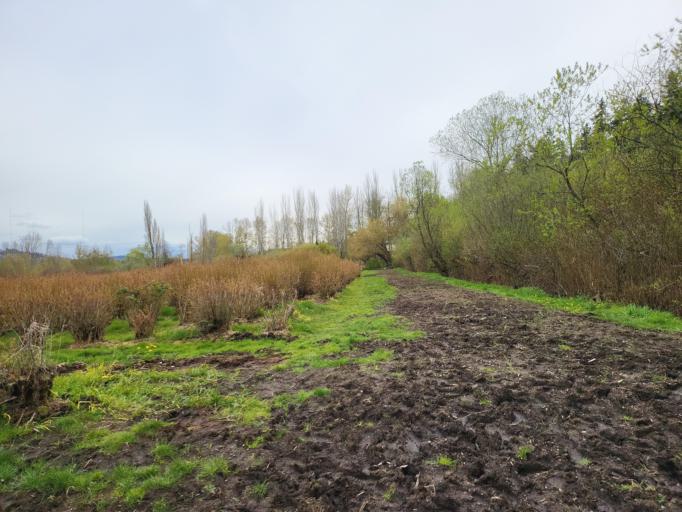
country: US
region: Washington
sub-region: King County
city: Bellevue
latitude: 47.5907
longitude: -122.1911
